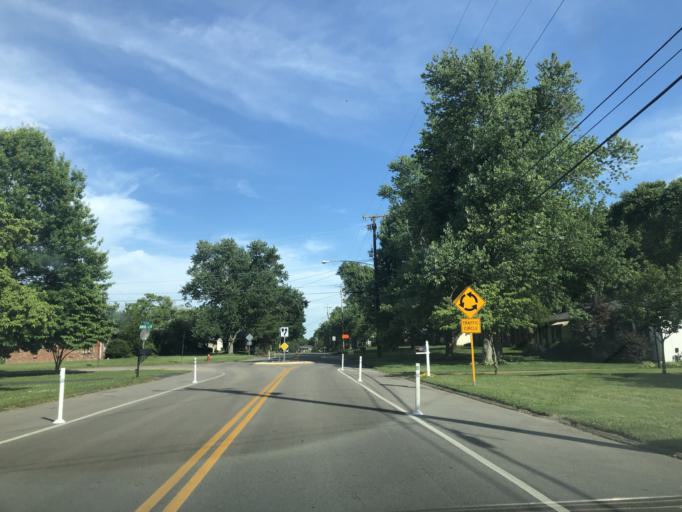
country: US
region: Tennessee
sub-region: Davidson County
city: Belle Meade
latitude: 36.0618
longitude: -86.9379
